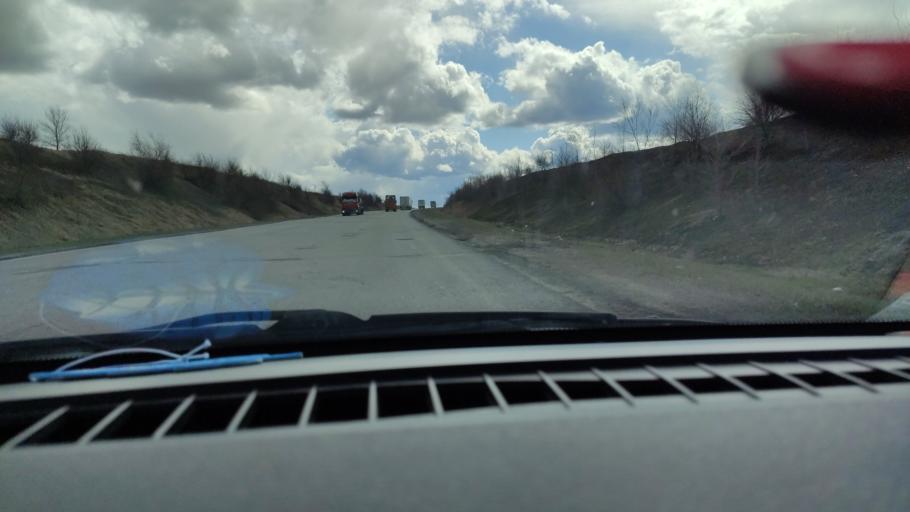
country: RU
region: Samara
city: Varlamovo
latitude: 53.0625
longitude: 48.3522
